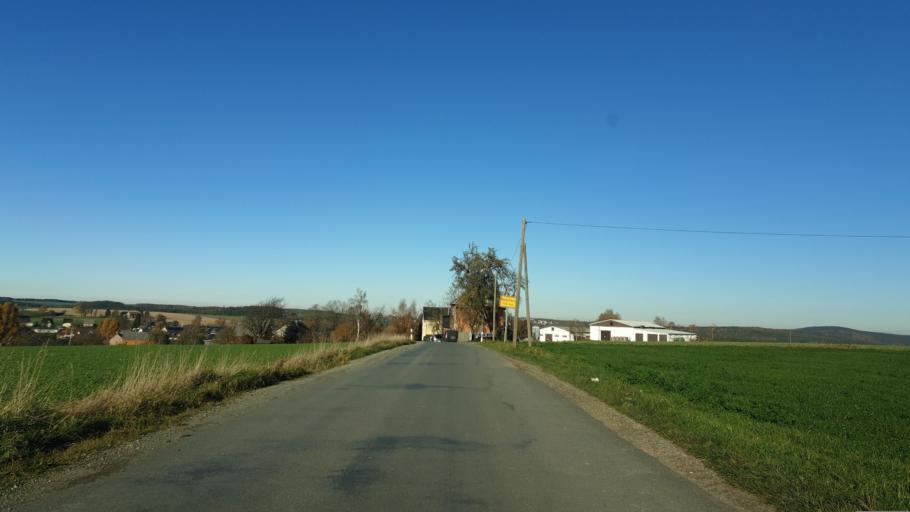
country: DE
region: Saxony
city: Elsterberg
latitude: 50.6333
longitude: 12.1546
